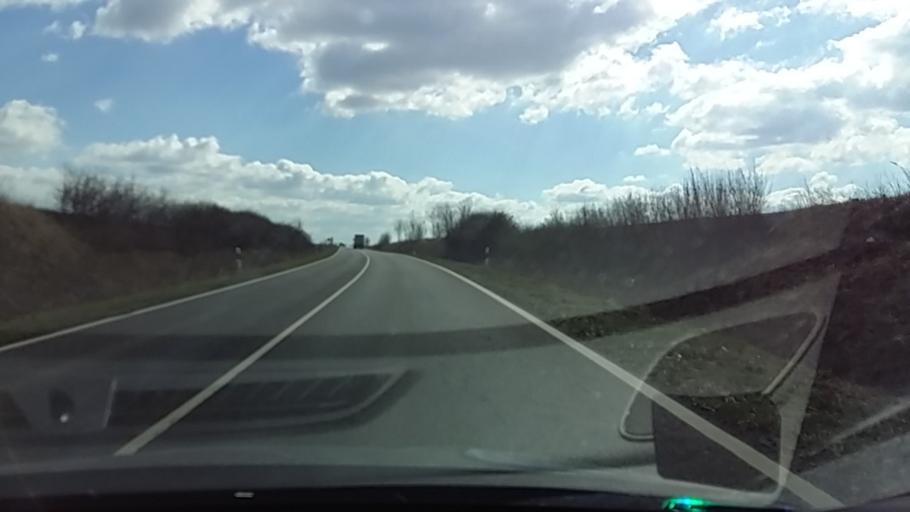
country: HU
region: Baranya
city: Kozarmisleny
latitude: 46.0427
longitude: 18.2718
